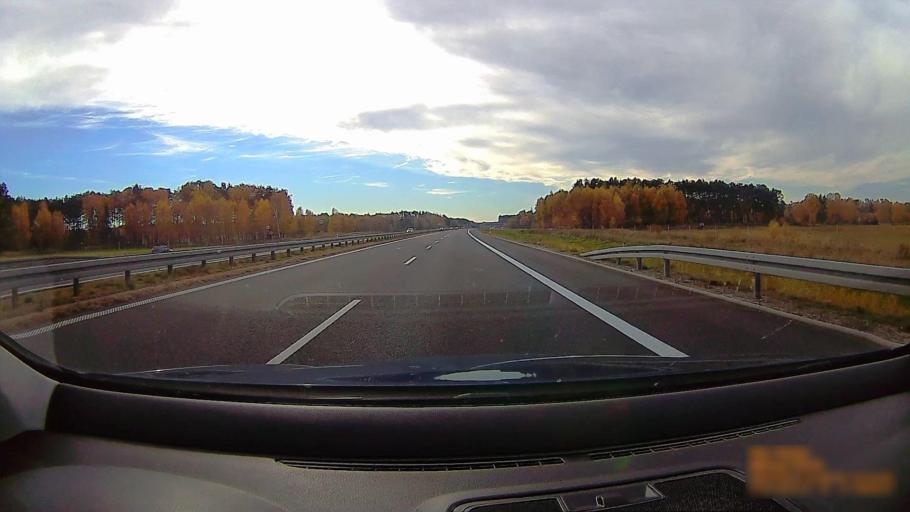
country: PL
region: Greater Poland Voivodeship
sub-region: Powiat ostrowski
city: Przygodzice
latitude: 51.5740
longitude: 17.8488
